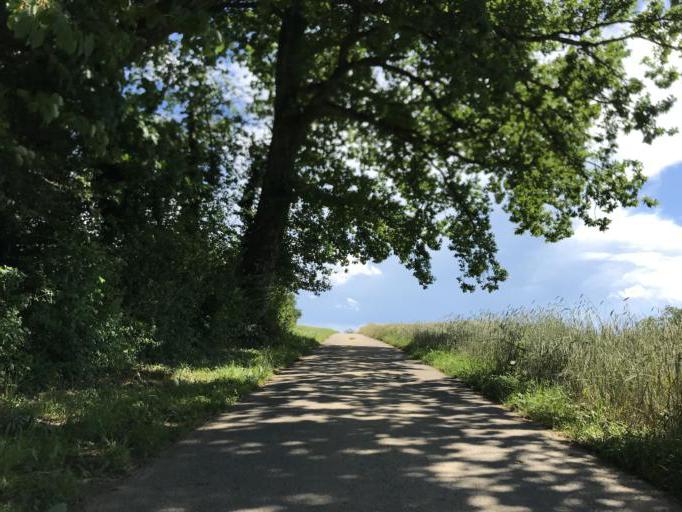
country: DE
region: Baden-Wuerttemberg
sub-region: Freiburg Region
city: Schopfheim
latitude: 47.6378
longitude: 7.8300
